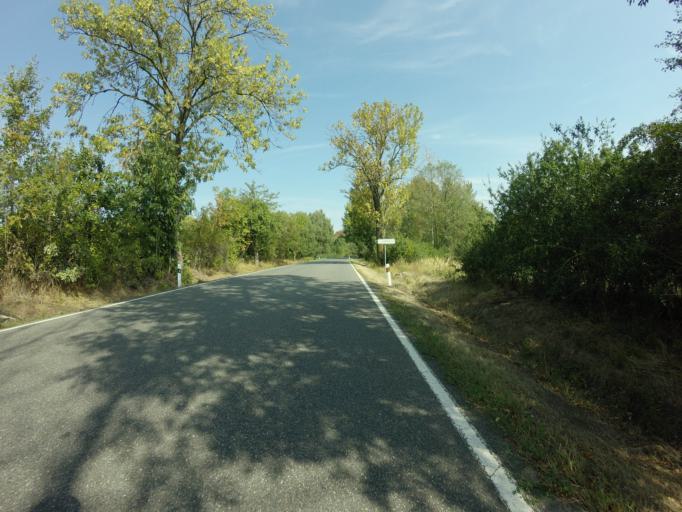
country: CZ
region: Central Bohemia
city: Sedlcany
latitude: 49.6107
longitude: 14.3847
